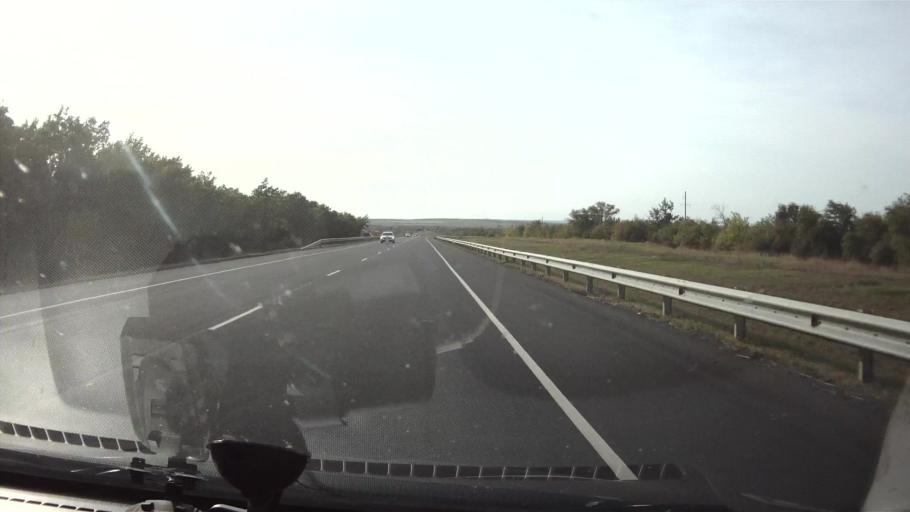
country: RU
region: Saratov
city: Yelshanka
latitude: 51.8265
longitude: 46.2756
